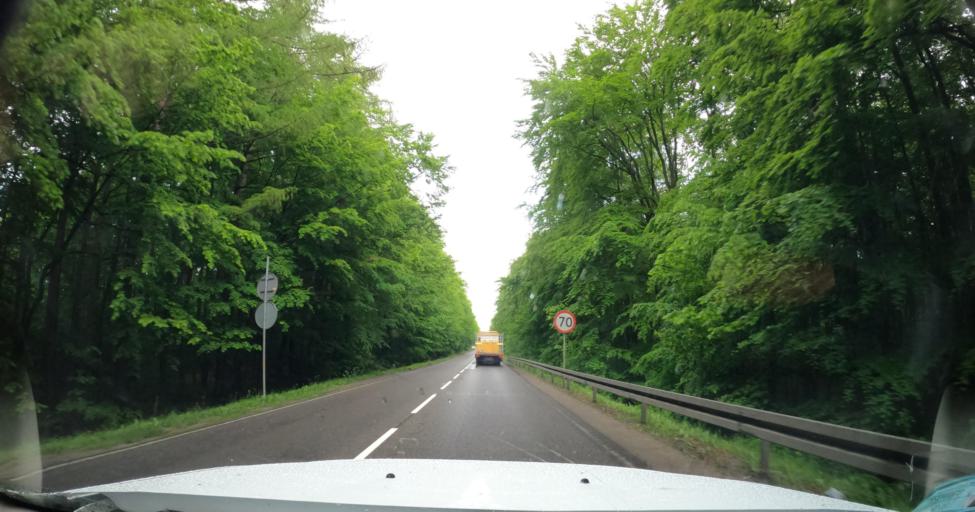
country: PL
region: Pomeranian Voivodeship
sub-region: Powiat kartuski
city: Kartuzy
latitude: 54.3292
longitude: 18.2188
